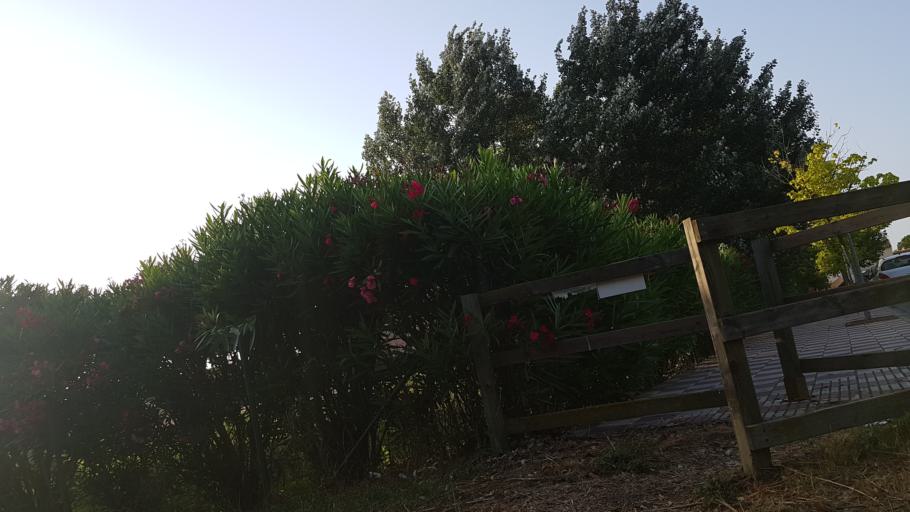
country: ES
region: Catalonia
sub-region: Provincia de Girona
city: Pals
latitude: 42.0069
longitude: 3.1916
